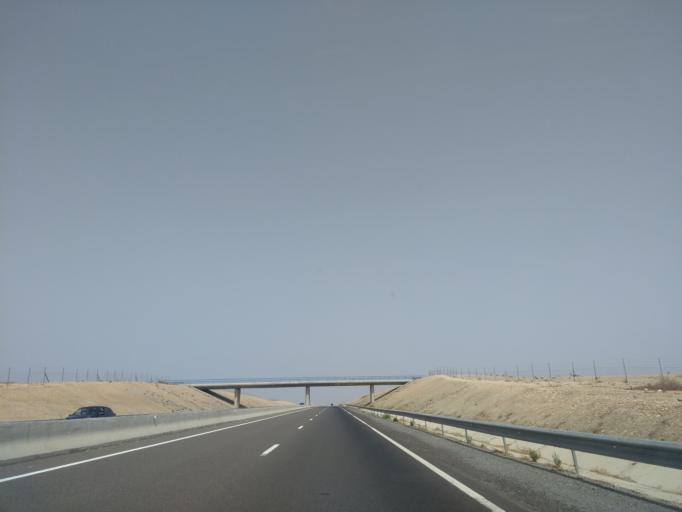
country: MA
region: Marrakech-Tensift-Al Haouz
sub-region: Chichaoua
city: Chichaoua
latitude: 31.5314
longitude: -8.4906
